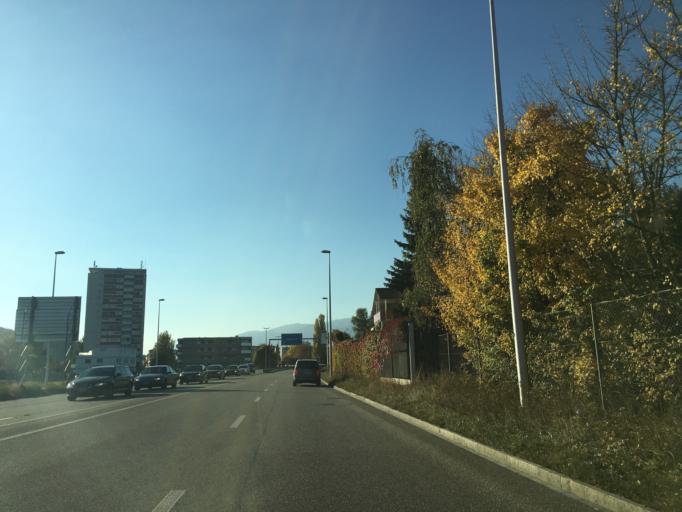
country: CH
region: Solothurn
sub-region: Bezirk Wasseramt
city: Zuchwil
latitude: 47.2036
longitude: 7.5672
